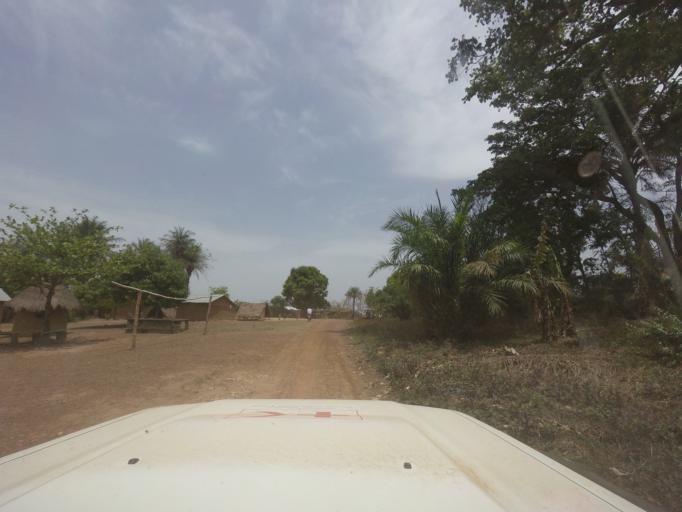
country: SL
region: Eastern Province
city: Buedu
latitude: 8.4852
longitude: -10.3340
